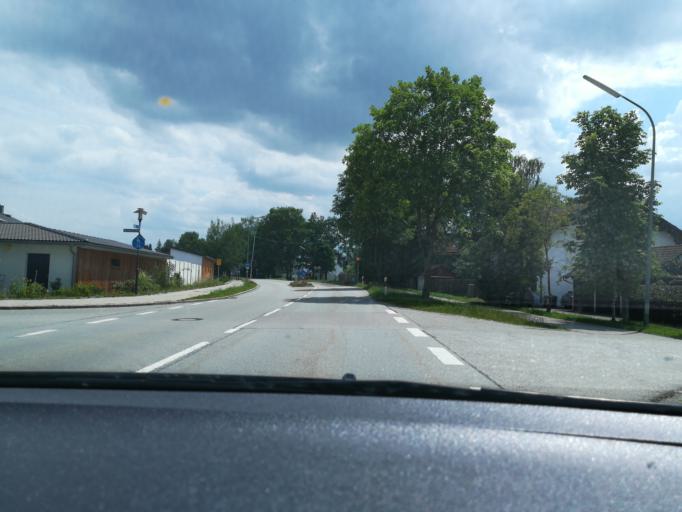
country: DE
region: Bavaria
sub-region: Upper Bavaria
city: Hohenkirchen-Siegertsbrunn
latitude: 48.0223
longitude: 11.7024
